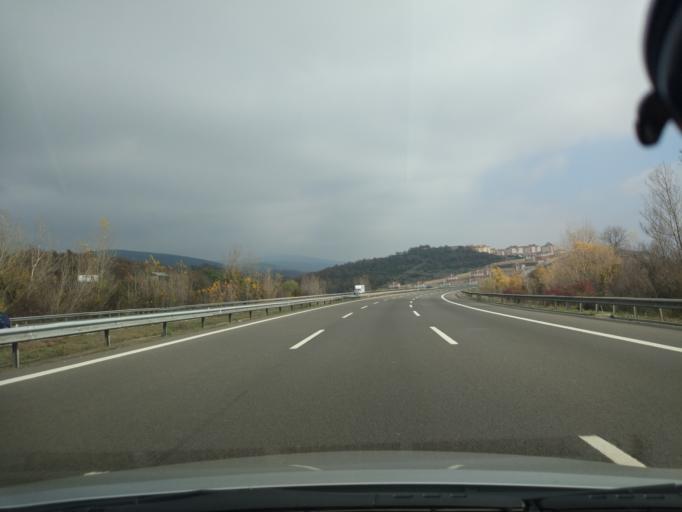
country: TR
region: Bolu
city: Bolu
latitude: 40.7391
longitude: 31.5381
